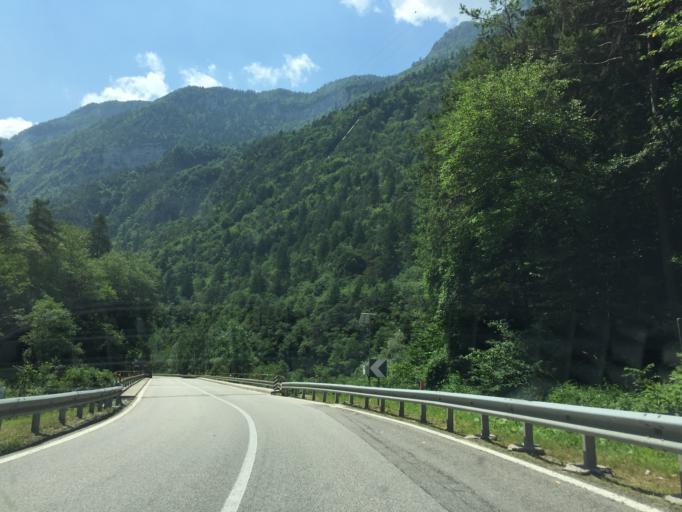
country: IT
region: Trentino-Alto Adige
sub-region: Provincia di Trento
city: Imer
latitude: 46.1380
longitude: 11.7706
